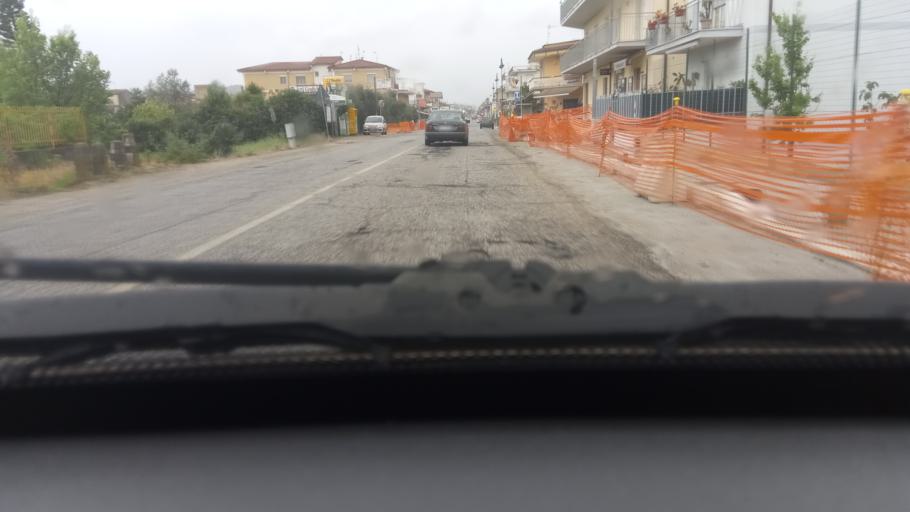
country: IT
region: Latium
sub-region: Provincia di Latina
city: Minturno
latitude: 41.2525
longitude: 13.7252
